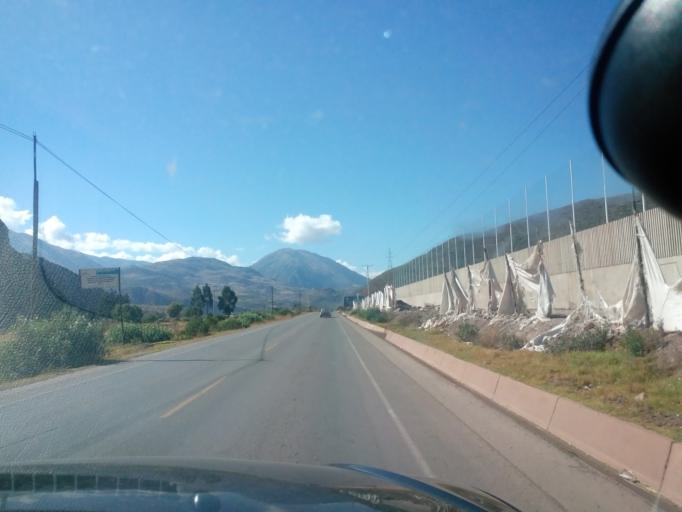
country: PE
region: Cusco
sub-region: Provincia de Quispicanchis
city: Oropesa
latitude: -13.6053
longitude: -71.7547
